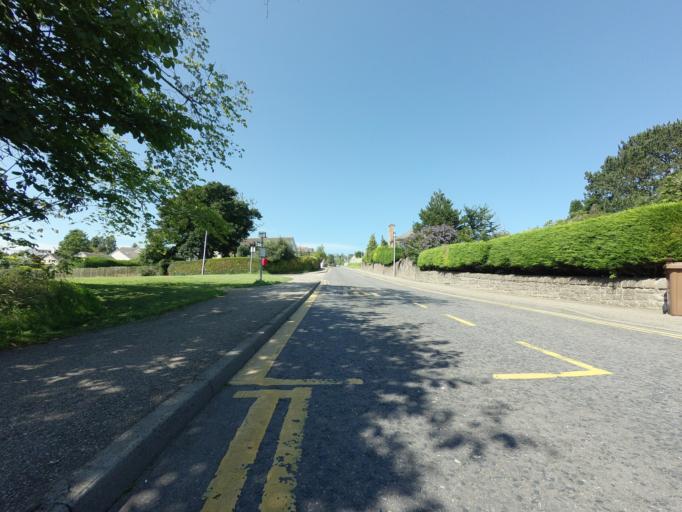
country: GB
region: Scotland
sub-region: Highland
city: Dingwall
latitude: 57.6015
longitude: -4.4289
